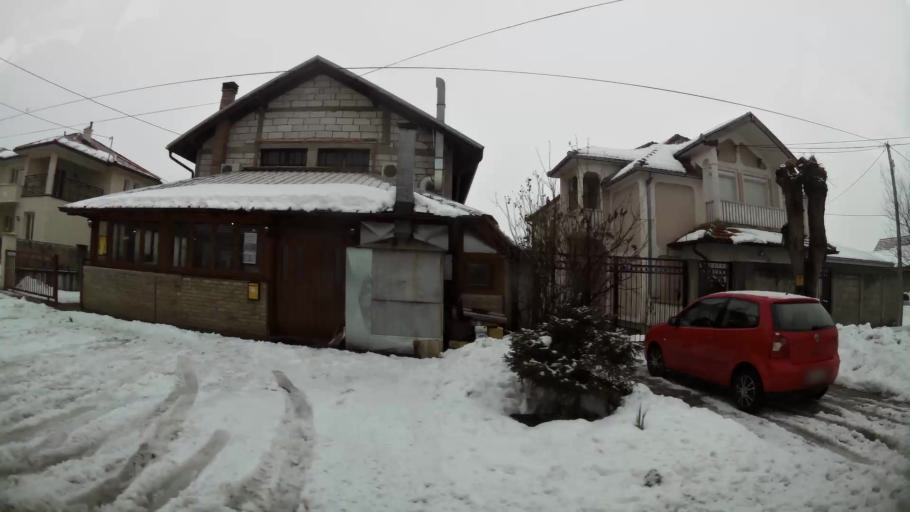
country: RS
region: Central Serbia
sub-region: Belgrade
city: Zemun
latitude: 44.8487
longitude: 20.3427
